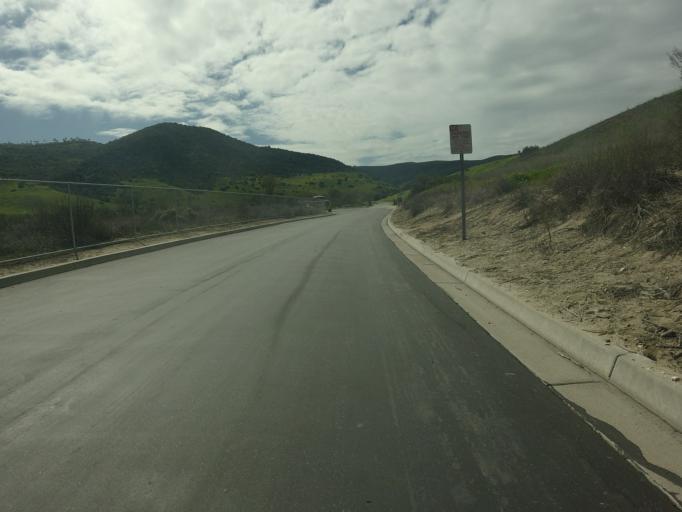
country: US
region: California
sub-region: Orange County
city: Aliso Viejo
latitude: 33.5451
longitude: -117.7263
